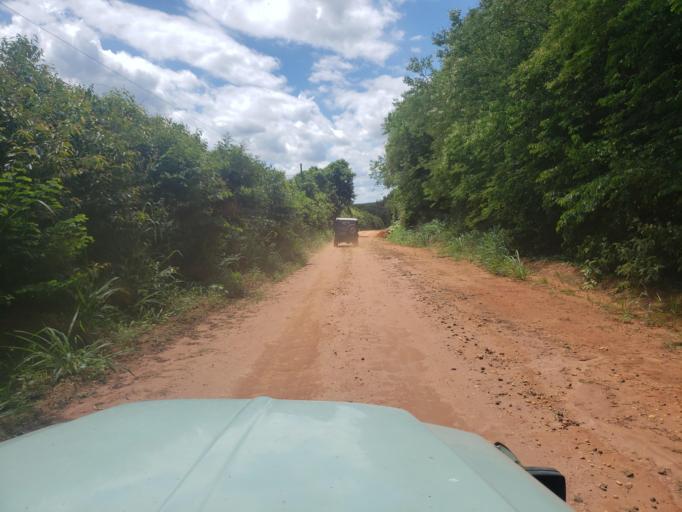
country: BR
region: Sao Paulo
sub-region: Conchal
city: Conchal
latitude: -22.2534
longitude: -47.0769
